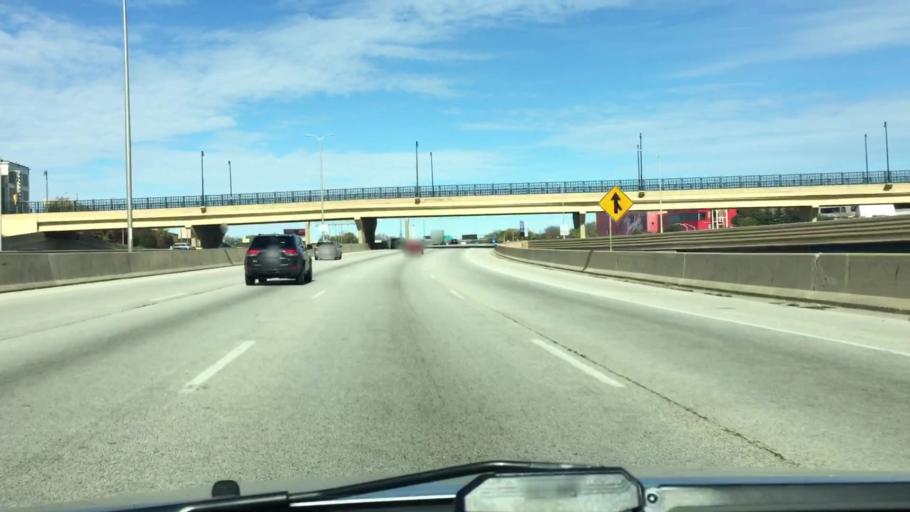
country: US
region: Wisconsin
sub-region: Milwaukee County
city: Milwaukee
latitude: 43.0471
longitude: -87.9264
